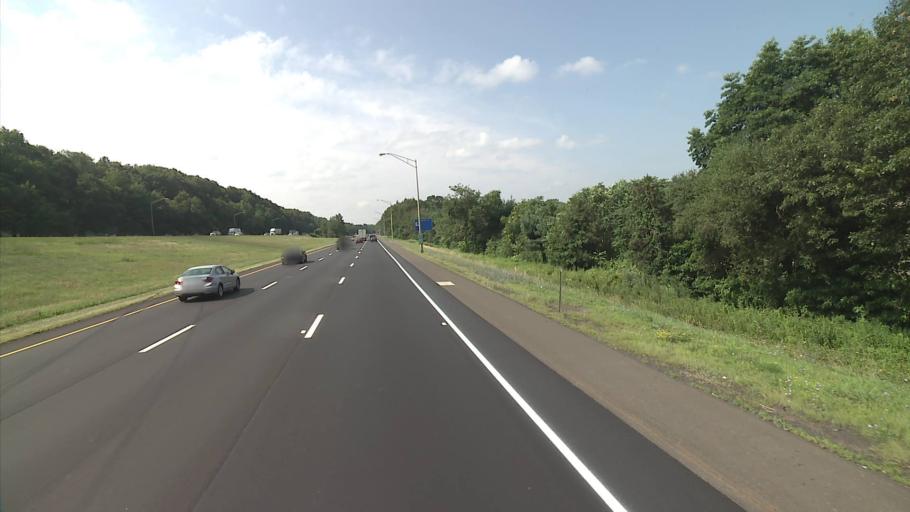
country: US
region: Connecticut
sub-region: New Haven County
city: North Haven
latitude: 41.4142
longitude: -72.8307
